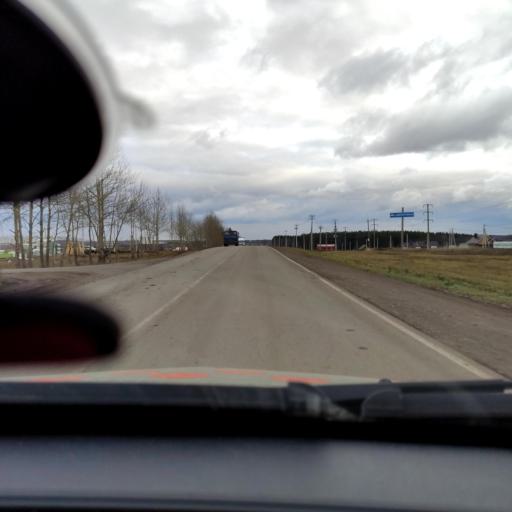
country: RU
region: Bashkortostan
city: Kabakovo
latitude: 54.6144
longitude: 56.1485
